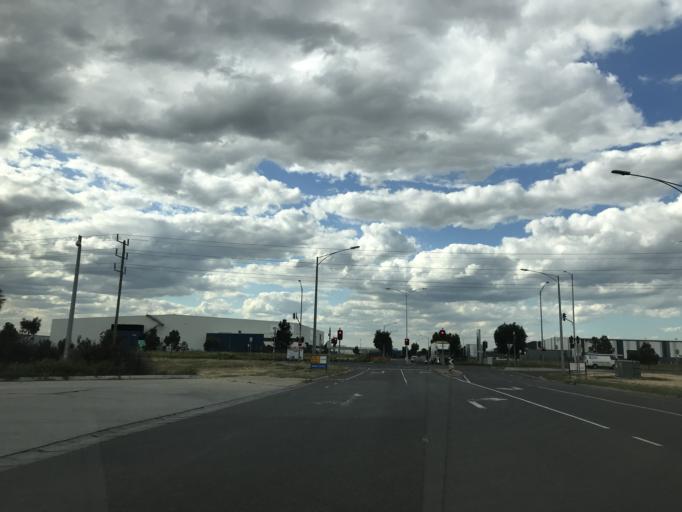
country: AU
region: Victoria
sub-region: Wyndham
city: Truganina
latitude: -37.8248
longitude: 144.7373
